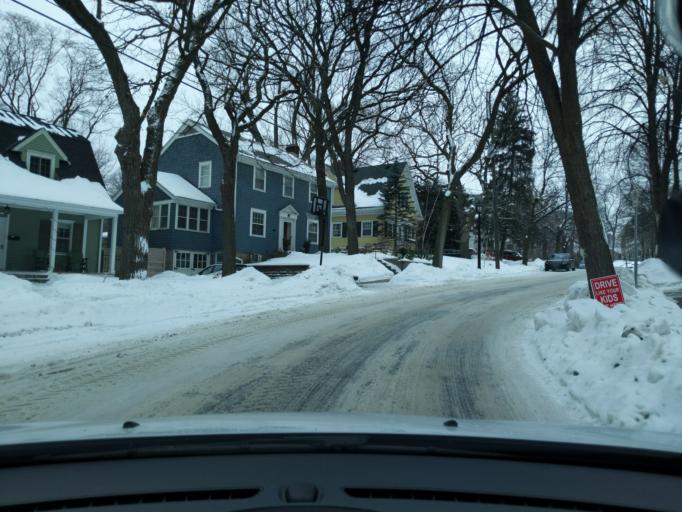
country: US
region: Minnesota
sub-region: Ramsey County
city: Lauderdale
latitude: 44.9664
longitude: -93.2118
